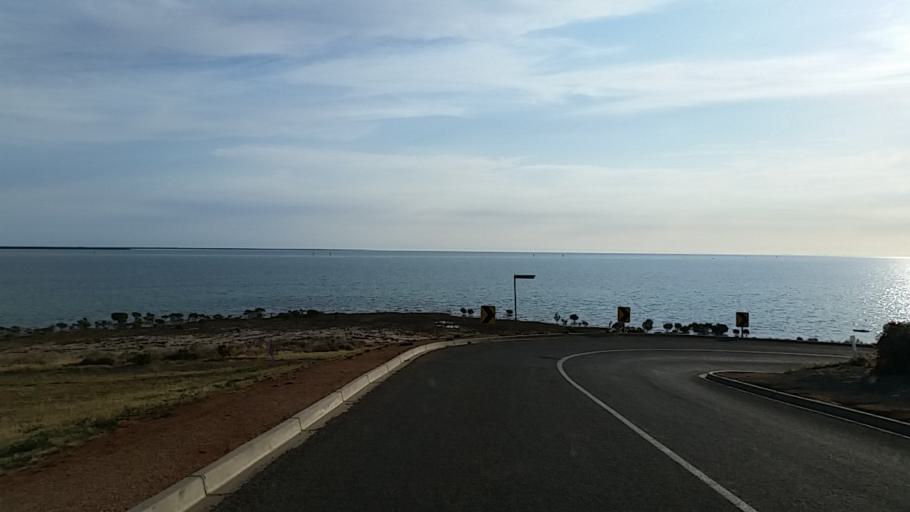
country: AU
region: South Australia
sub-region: Port Pirie City and Dists
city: Port Pirie
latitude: -33.1049
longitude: 138.0261
